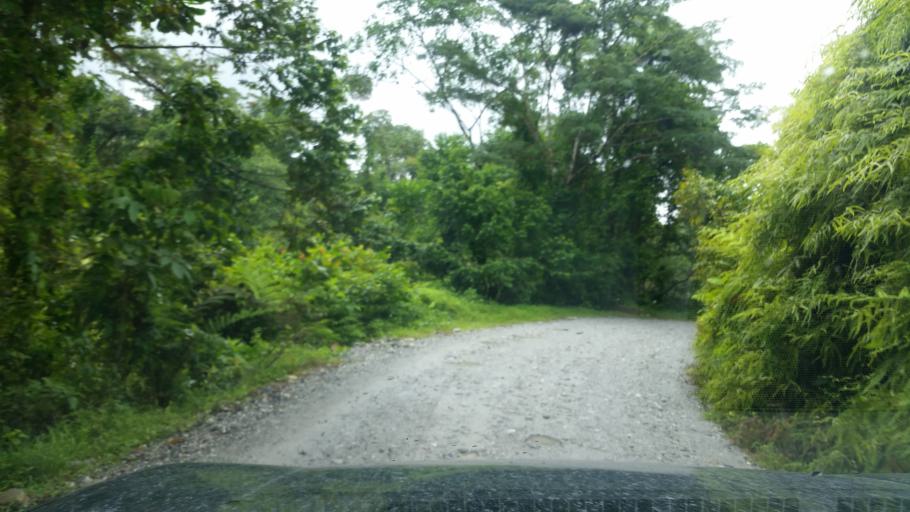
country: NI
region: Atlantico Norte (RAAN)
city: Bonanza
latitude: 14.0617
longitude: -84.6202
